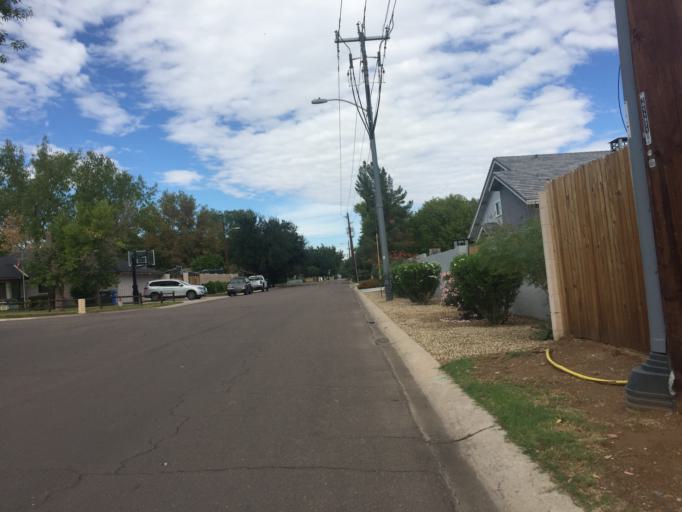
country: US
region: Arizona
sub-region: Maricopa County
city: Phoenix
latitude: 33.5339
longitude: -112.0693
